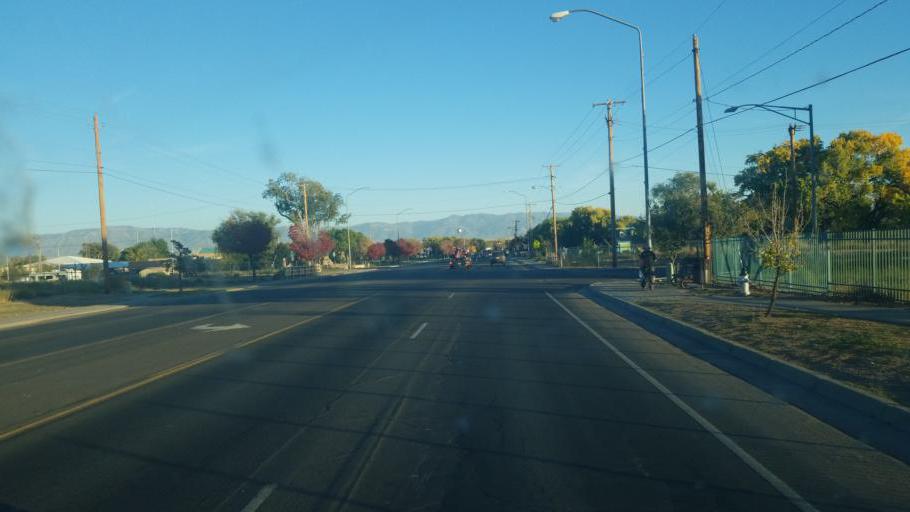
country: US
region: New Mexico
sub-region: Valencia County
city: Los Lunas
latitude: 34.8126
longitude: -106.7443
